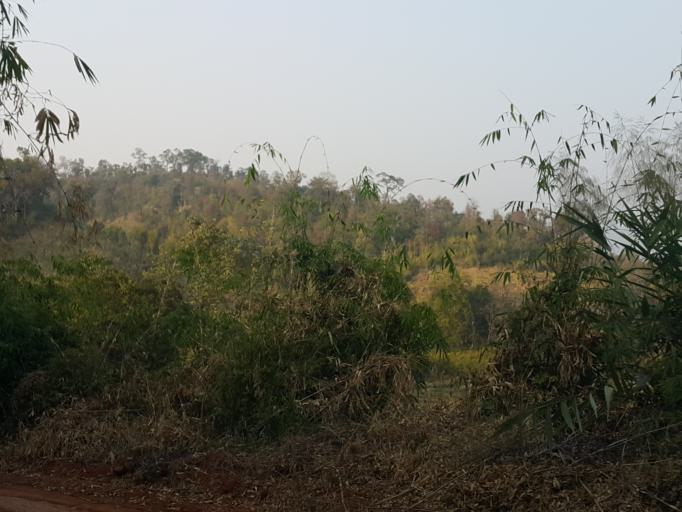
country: TH
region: Chiang Mai
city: Mae Taeng
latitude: 19.0532
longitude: 98.7660
